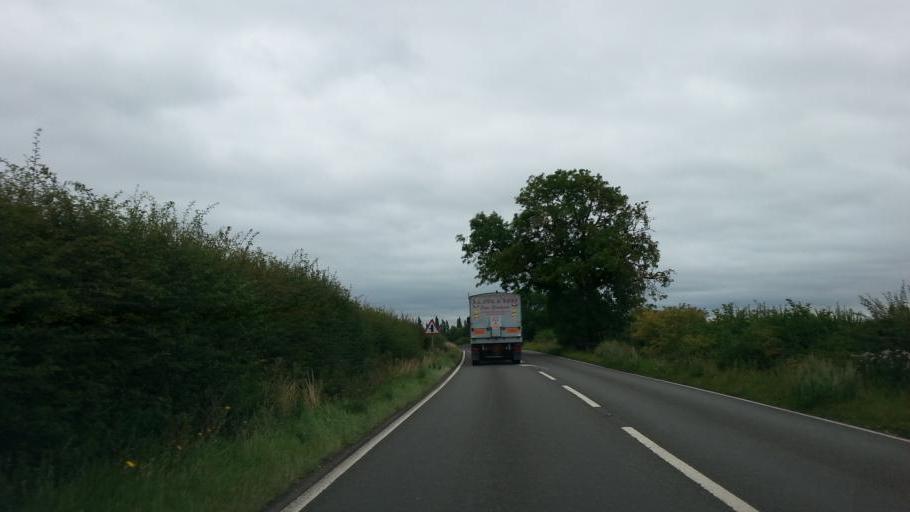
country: GB
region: England
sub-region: Nottinghamshire
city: Southwell
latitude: 53.1068
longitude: -0.9556
